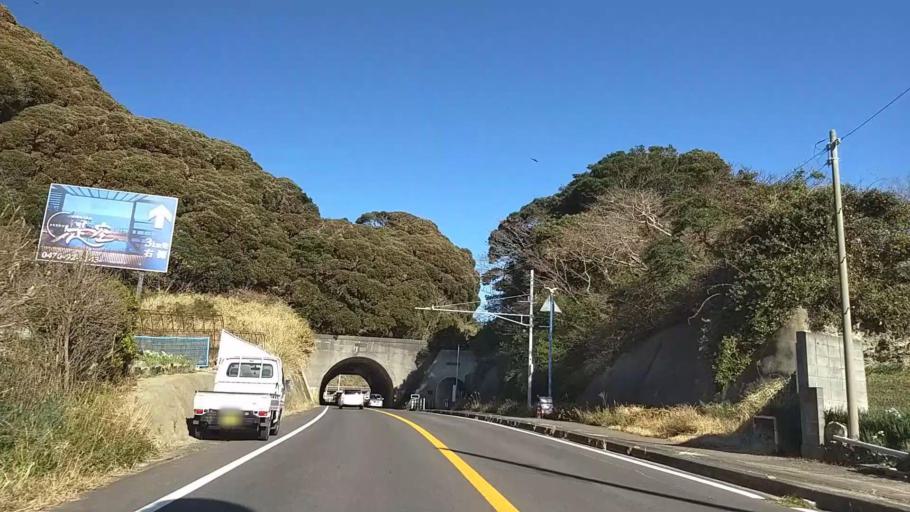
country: JP
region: Chiba
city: Kawaguchi
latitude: 35.0655
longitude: 140.0774
